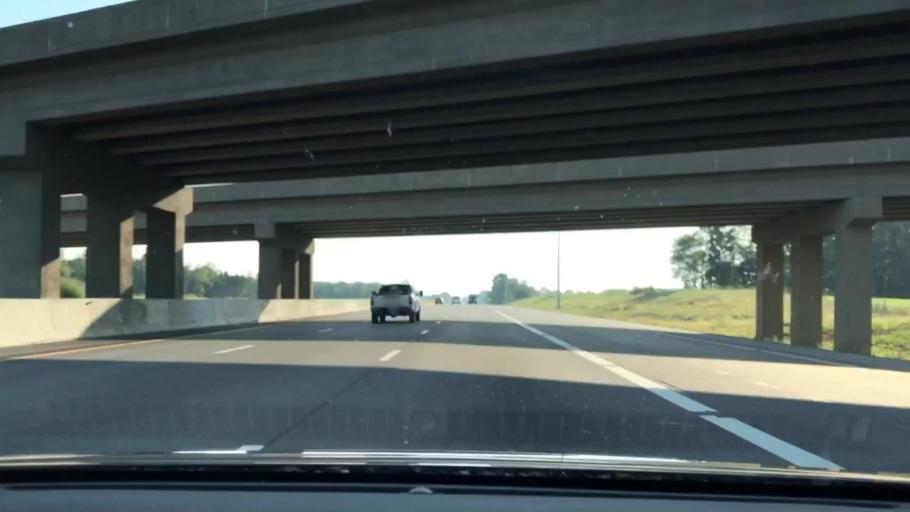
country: US
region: Kentucky
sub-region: Warren County
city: Bowling Green
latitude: 37.0116
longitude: -86.3271
